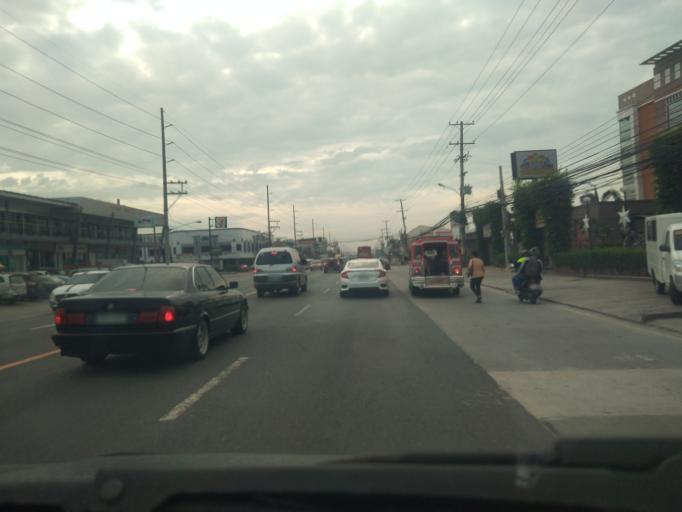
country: PH
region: Central Luzon
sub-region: Province of Pampanga
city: Bulaon
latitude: 15.0685
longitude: 120.6487
